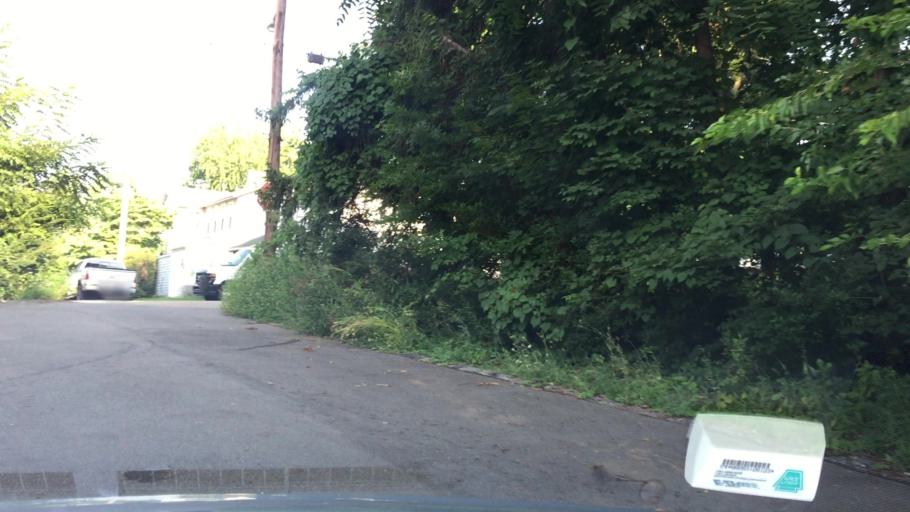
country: US
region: Pennsylvania
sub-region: Allegheny County
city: Emsworth
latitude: 40.5123
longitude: -80.0989
